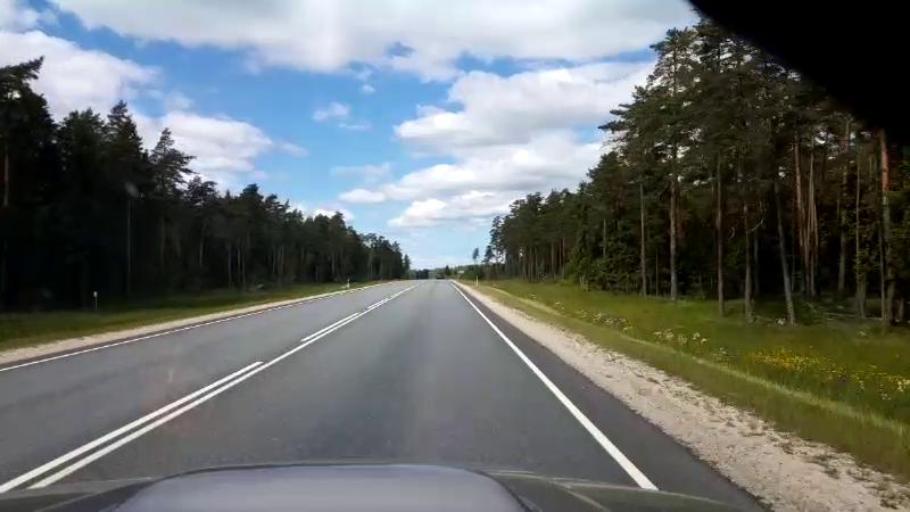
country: EE
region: Raplamaa
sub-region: Maerjamaa vald
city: Marjamaa
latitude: 59.0207
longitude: 24.4509
